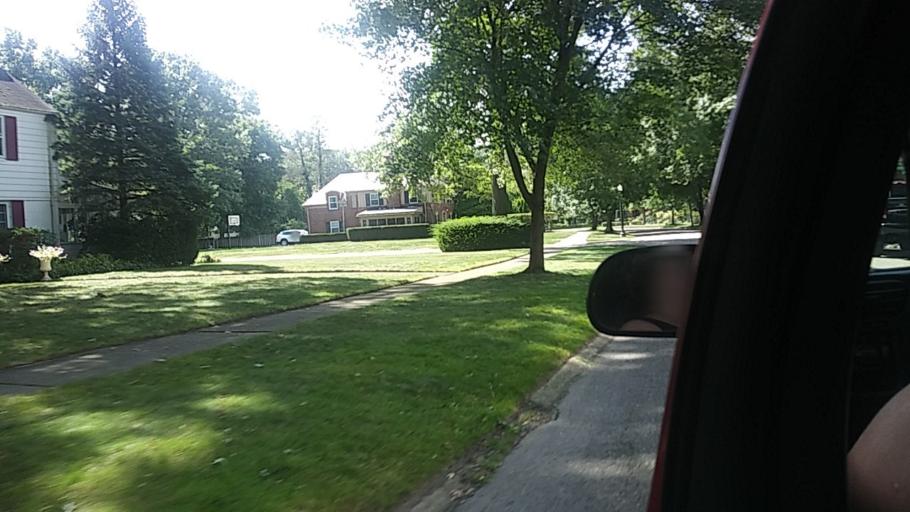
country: US
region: Ohio
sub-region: Summit County
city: Akron
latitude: 41.1011
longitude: -81.5609
